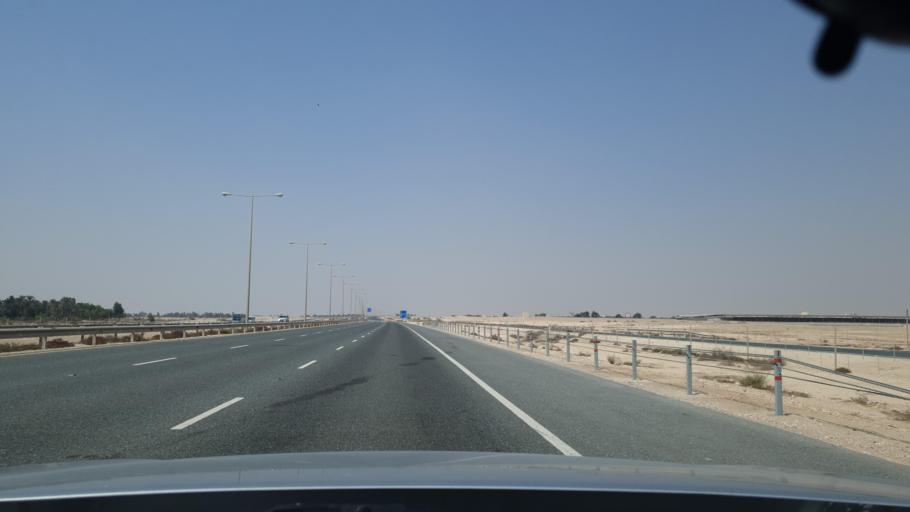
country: QA
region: Al Khawr
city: Al Khawr
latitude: 25.7780
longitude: 51.4065
